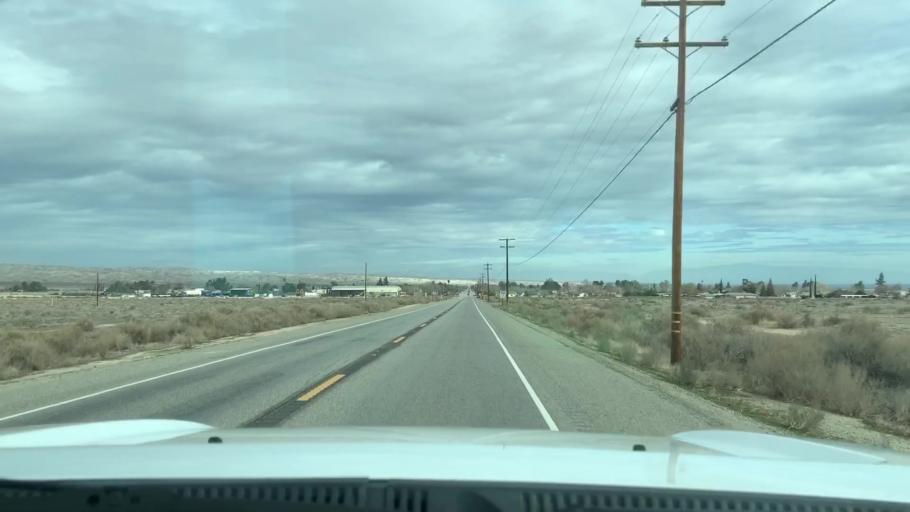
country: US
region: California
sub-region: Kern County
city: Ford City
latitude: 35.2020
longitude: -119.4164
